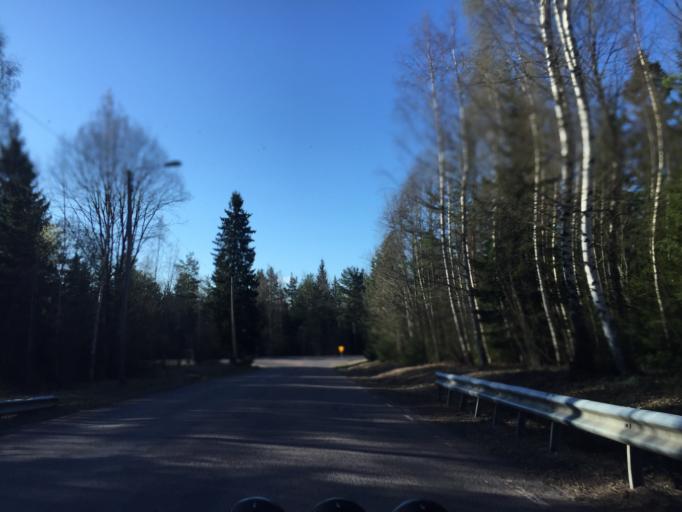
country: SE
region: Dalarna
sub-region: Borlange Kommun
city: Borlaenge
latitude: 60.4699
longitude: 15.3841
